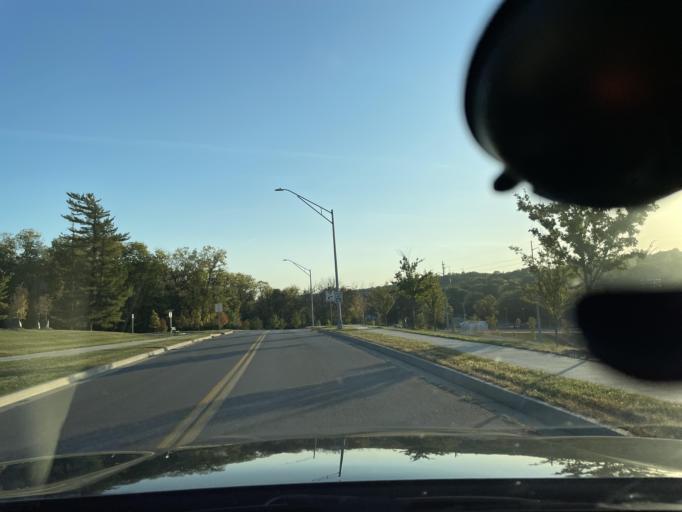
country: US
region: Missouri
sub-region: Buchanan County
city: Saint Joseph
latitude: 39.7988
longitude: -94.8409
